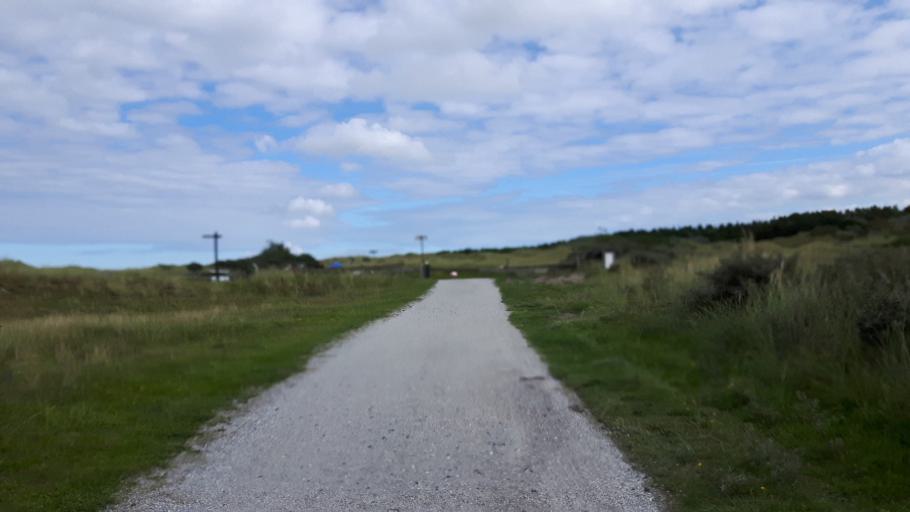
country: NL
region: Friesland
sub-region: Gemeente Ameland
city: Nes
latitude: 53.4577
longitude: 5.7572
